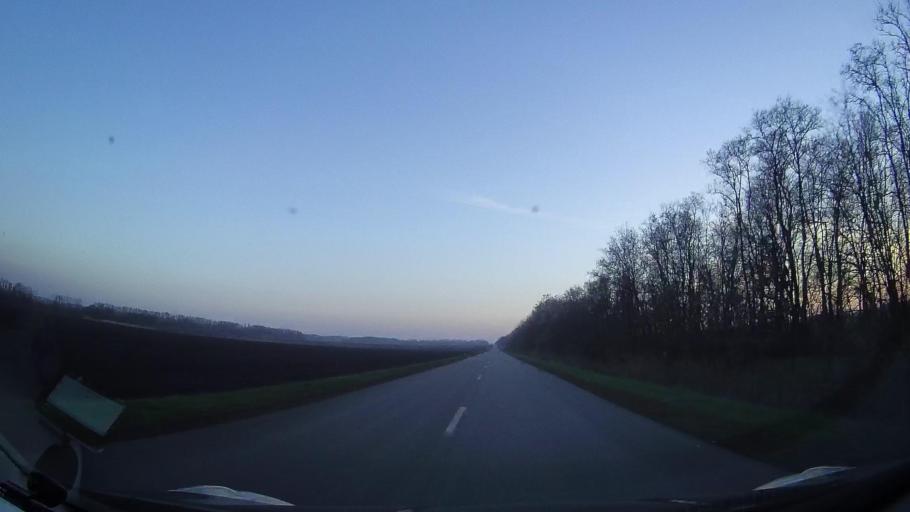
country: RU
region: Rostov
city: Zernograd
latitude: 47.0067
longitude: 40.3916
